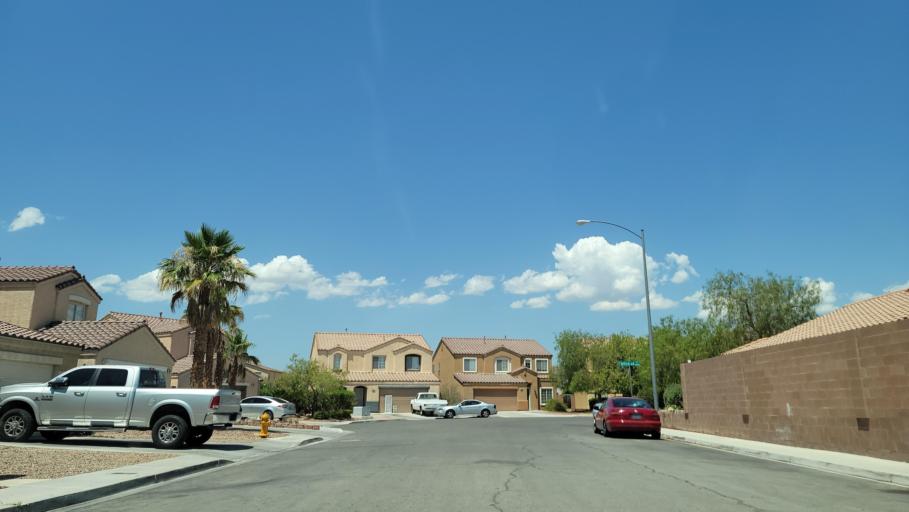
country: US
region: Nevada
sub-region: Clark County
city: Spring Valley
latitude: 36.0826
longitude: -115.2577
